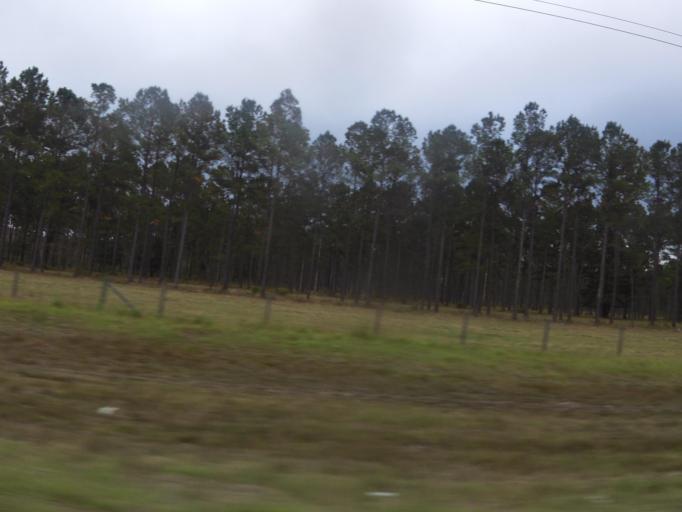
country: US
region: Georgia
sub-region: Charlton County
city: Folkston
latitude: 30.7575
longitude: -82.0701
